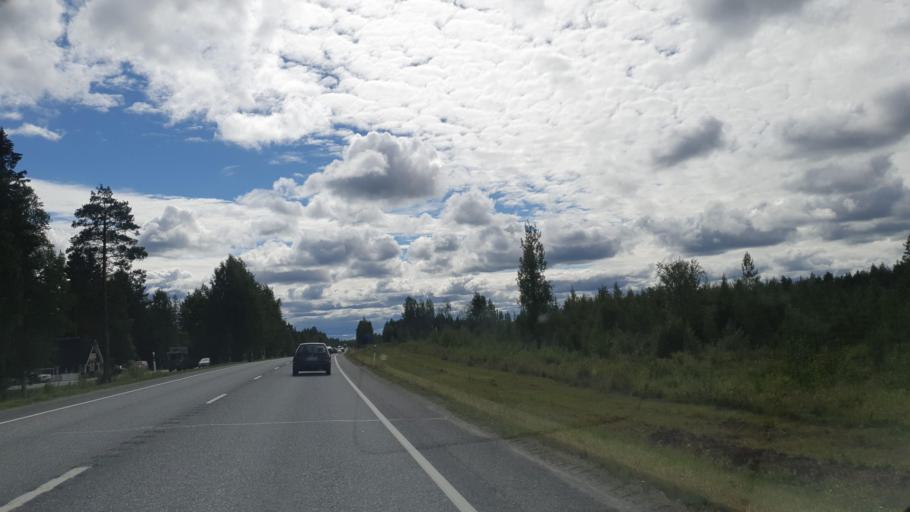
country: FI
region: Kainuu
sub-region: Kajaani
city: Kajaani
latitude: 64.1601
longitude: 27.5218
